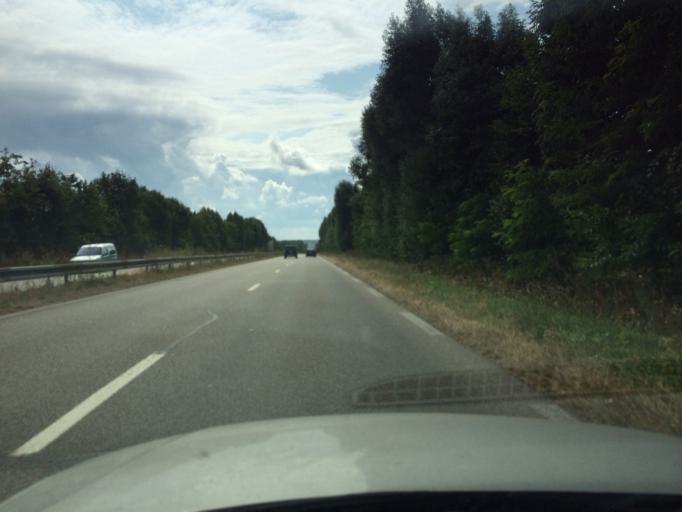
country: FR
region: Lower Normandy
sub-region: Departement de la Manche
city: Montebourg
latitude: 49.4870
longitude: -1.3985
